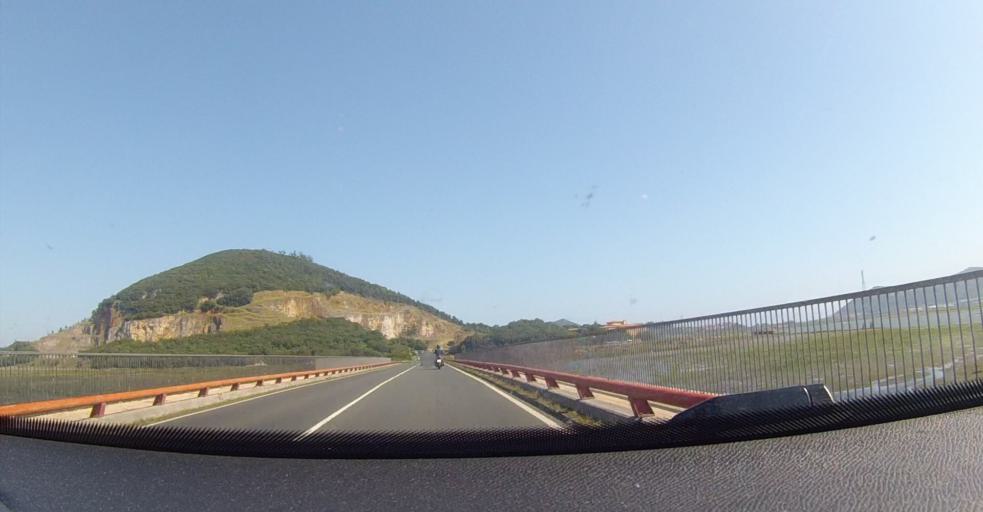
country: ES
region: Cantabria
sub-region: Provincia de Cantabria
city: Barcena de Cicero
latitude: 43.4242
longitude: -3.4911
